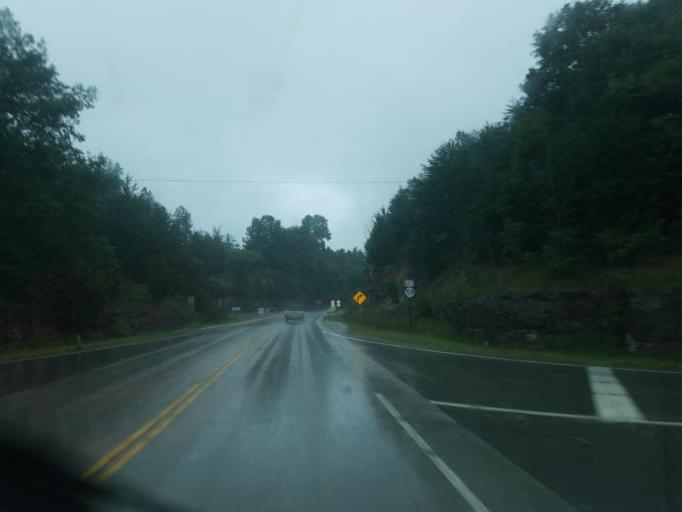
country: US
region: Kentucky
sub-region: Carter County
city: Olive Hill
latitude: 38.3321
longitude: -83.2090
